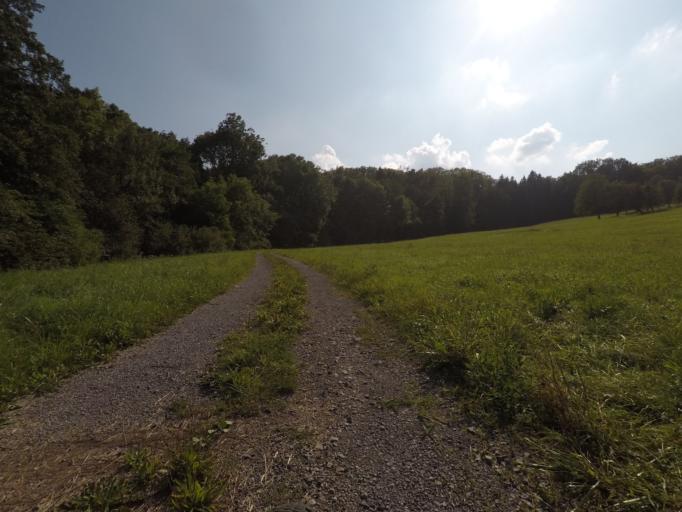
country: DE
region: Baden-Wuerttemberg
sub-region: Regierungsbezirk Stuttgart
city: Weil im Schonbuch
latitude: 48.6157
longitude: 9.0493
